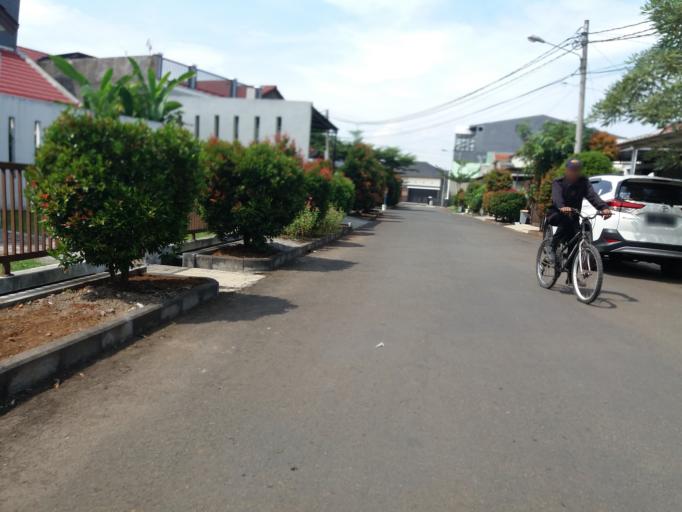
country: ID
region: West Java
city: Bandung
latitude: -6.9234
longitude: 107.6651
